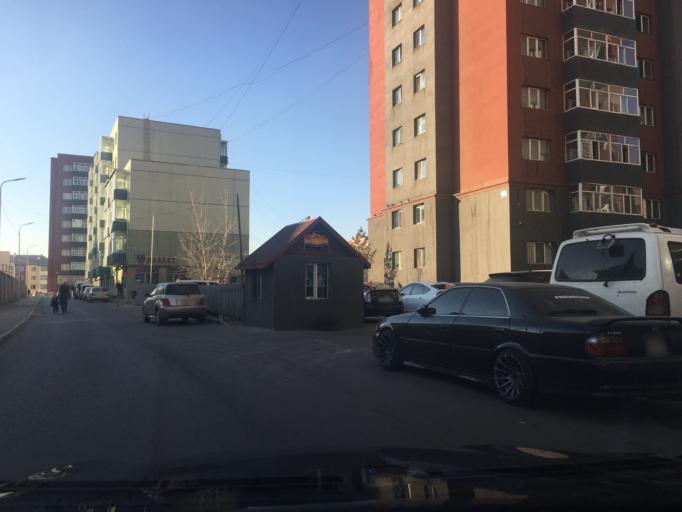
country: MN
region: Ulaanbaatar
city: Ulaanbaatar
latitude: 47.9171
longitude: 106.8747
